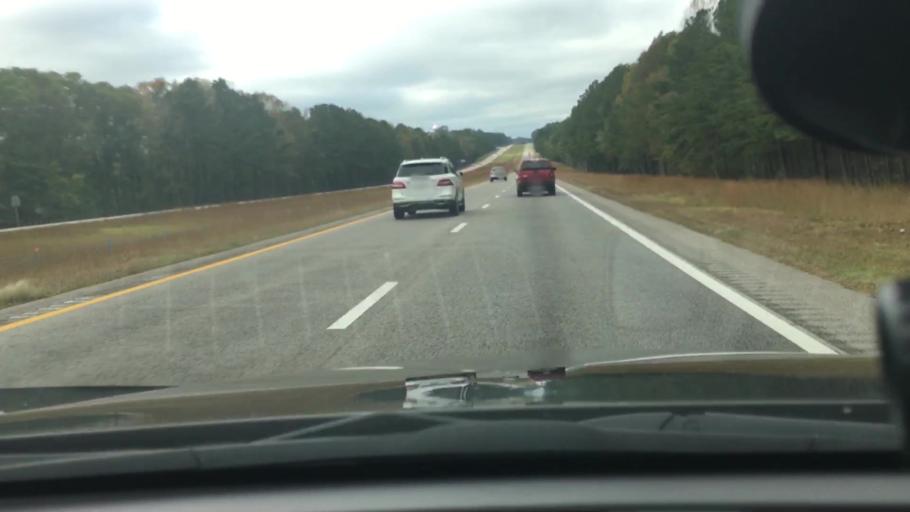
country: US
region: North Carolina
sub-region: Wake County
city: Zebulon
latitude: 35.8164
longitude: -78.2487
